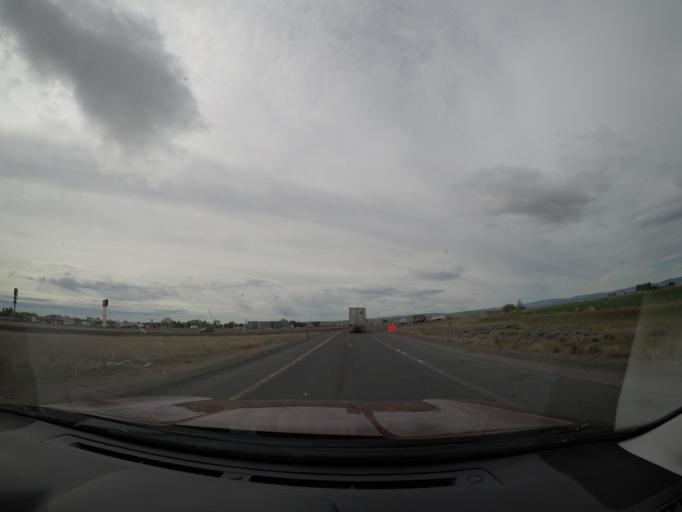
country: US
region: Washington
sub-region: Grant County
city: Quincy
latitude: 47.0849
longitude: -119.8632
